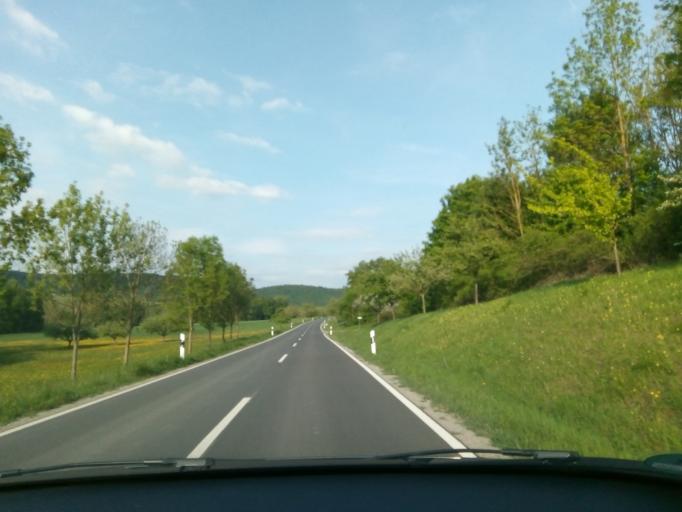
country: DE
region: Bavaria
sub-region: Regierungsbezirk Unterfranken
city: Oberschwarzach
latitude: 49.8670
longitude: 10.4251
